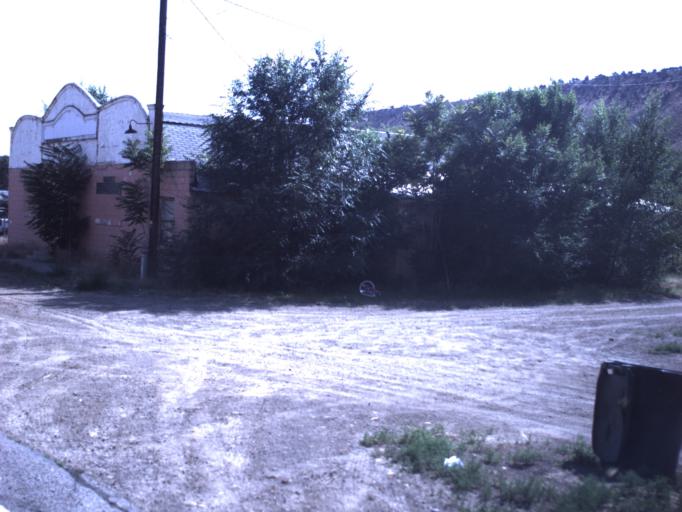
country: US
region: Utah
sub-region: Carbon County
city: Helper
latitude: 39.6721
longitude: -110.8598
